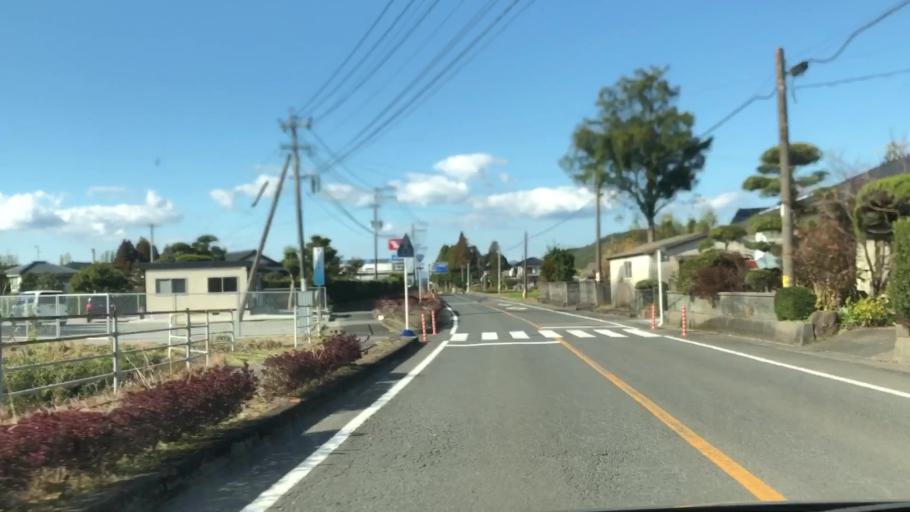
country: JP
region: Kagoshima
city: Satsumasendai
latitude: 31.7971
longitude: 130.4409
